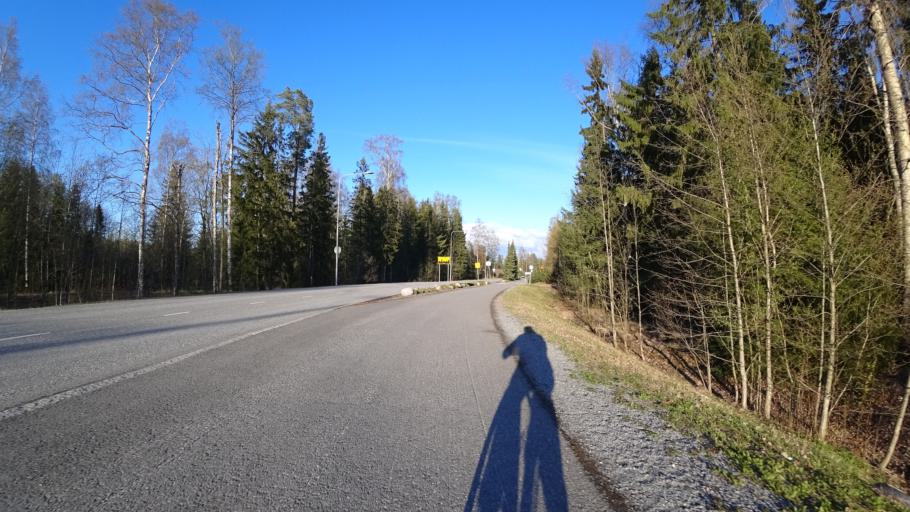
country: FI
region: Pirkanmaa
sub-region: Tampere
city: Yloejaervi
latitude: 61.4950
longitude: 23.5677
